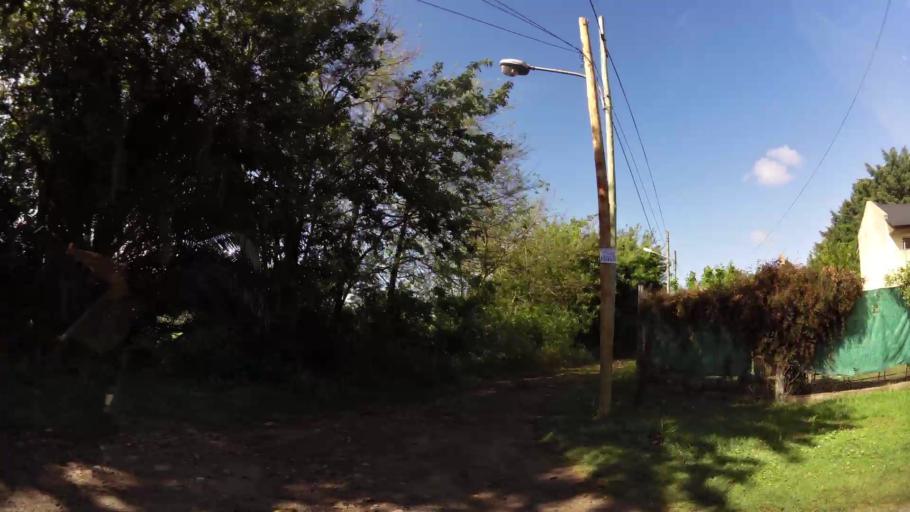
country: AR
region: Buenos Aires
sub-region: Partido de Quilmes
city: Quilmes
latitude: -34.7944
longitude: -58.1481
